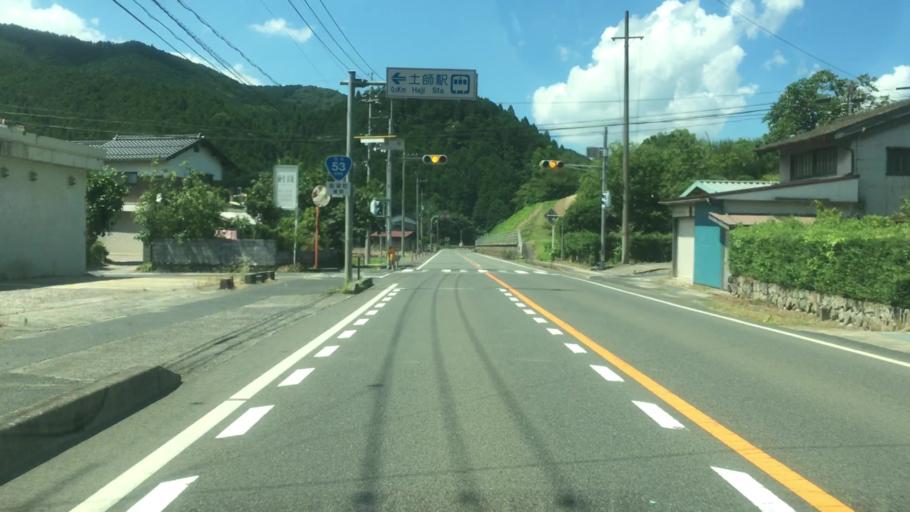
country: JP
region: Tottori
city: Tottori
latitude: 35.2346
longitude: 134.2275
